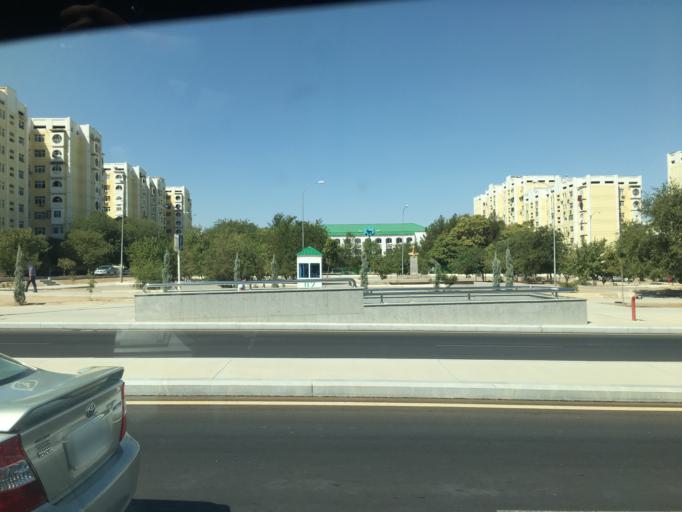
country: TM
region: Ahal
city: Ashgabat
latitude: 37.8994
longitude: 58.3885
